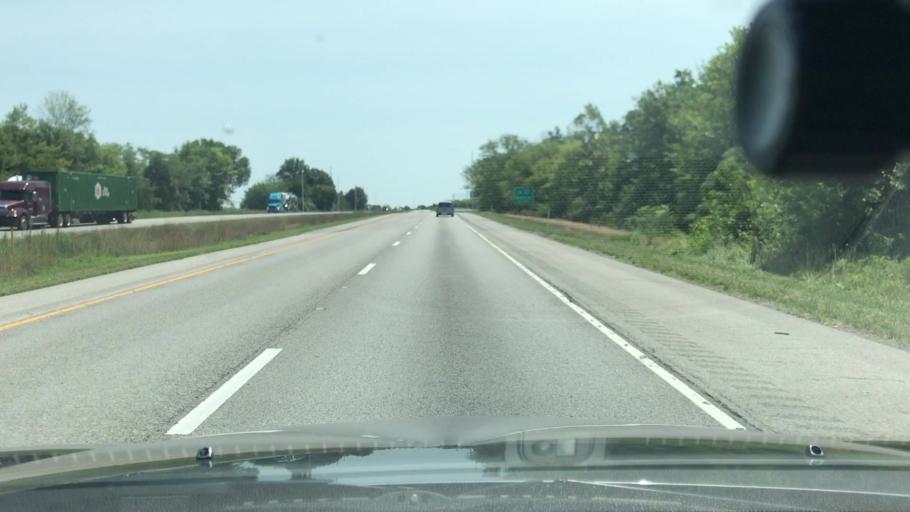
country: US
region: Illinois
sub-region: Jefferson County
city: Mount Vernon
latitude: 38.3407
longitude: -88.9657
